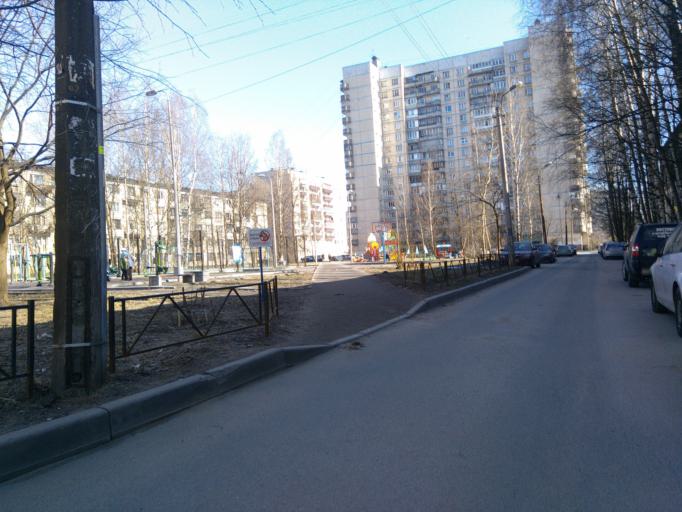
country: RU
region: St.-Petersburg
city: Grazhdanka
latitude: 60.0322
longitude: 30.4122
